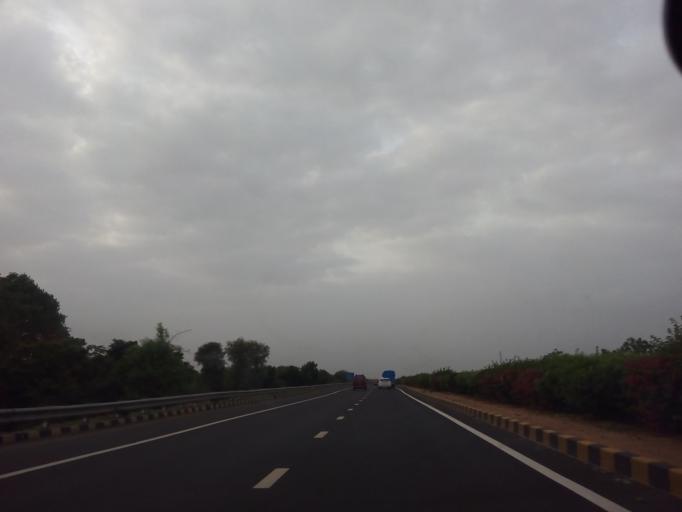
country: IN
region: Gujarat
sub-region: Kheda
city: Mahemdavad
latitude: 22.9128
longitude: 72.7633
